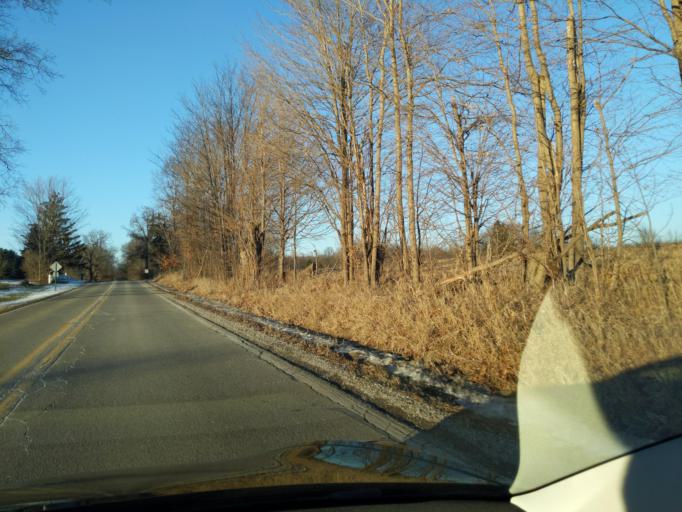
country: US
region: Michigan
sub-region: Ingham County
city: Stockbridge
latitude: 42.4491
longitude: -84.0761
